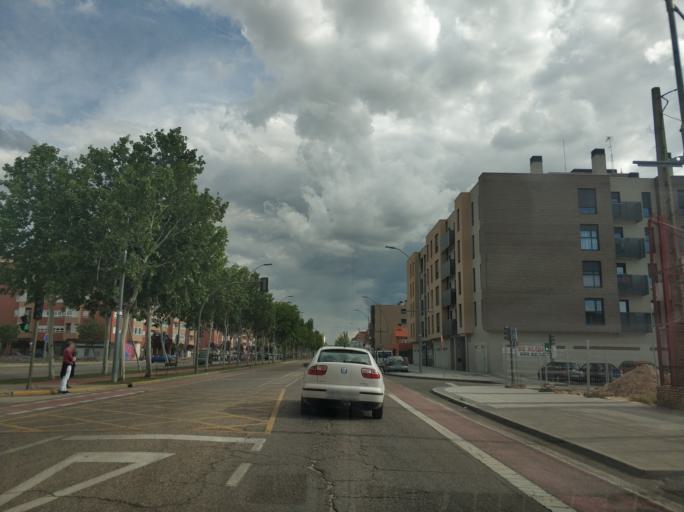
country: ES
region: Castille and Leon
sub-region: Provincia de Burgos
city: Aranda de Duero
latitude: 41.6649
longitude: -3.6913
